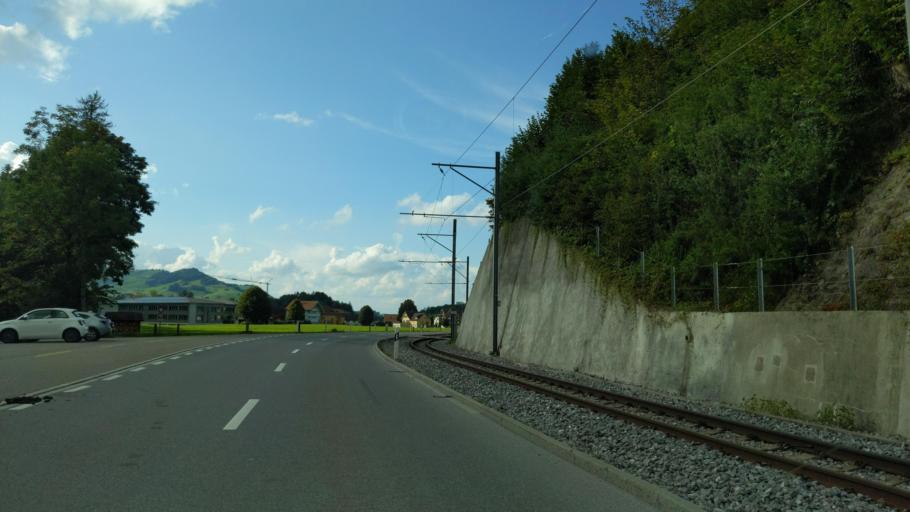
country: CH
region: Appenzell Innerrhoden
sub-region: Appenzell Inner Rhodes
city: Appenzell
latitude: 47.3182
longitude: 9.4326
